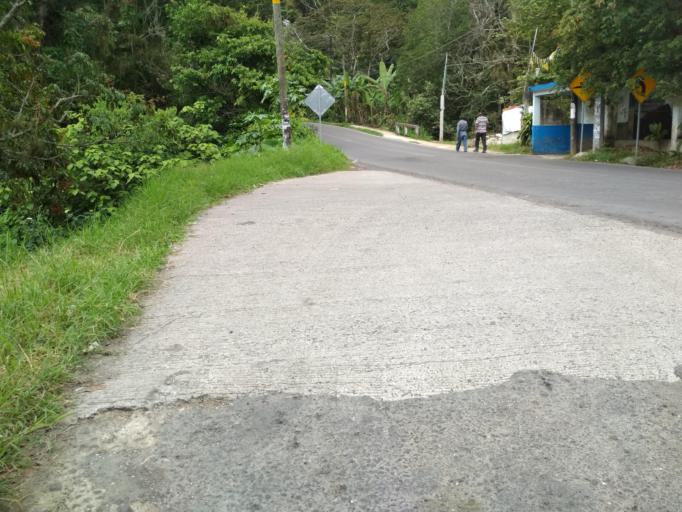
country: MX
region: Veracruz
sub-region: Jilotepec
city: El Pueblito (Garbanzal)
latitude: 19.6154
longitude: -96.9257
